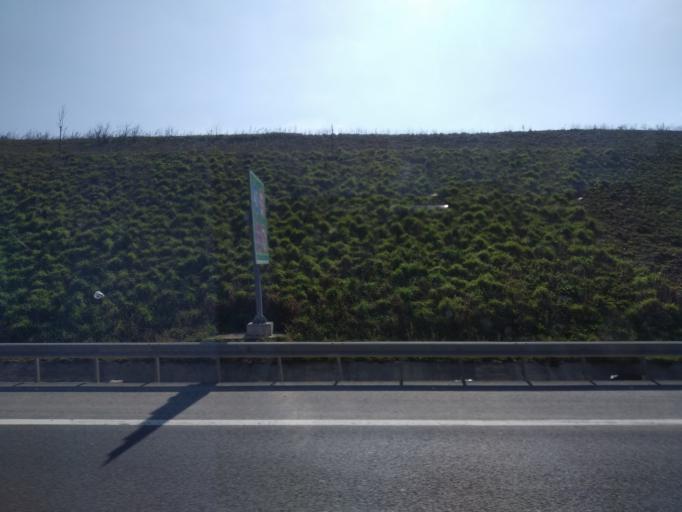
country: TR
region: Istanbul
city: Kemerburgaz
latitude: 41.2294
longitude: 28.8586
